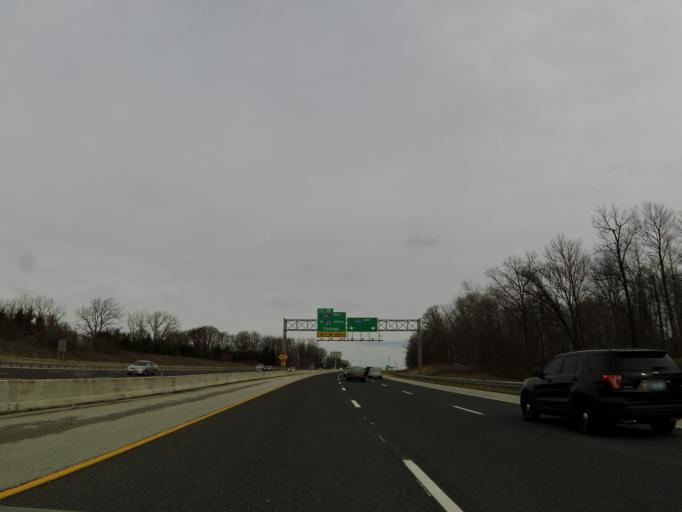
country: US
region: Indiana
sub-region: Boone County
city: Zionsville
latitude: 39.9184
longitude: -86.2696
